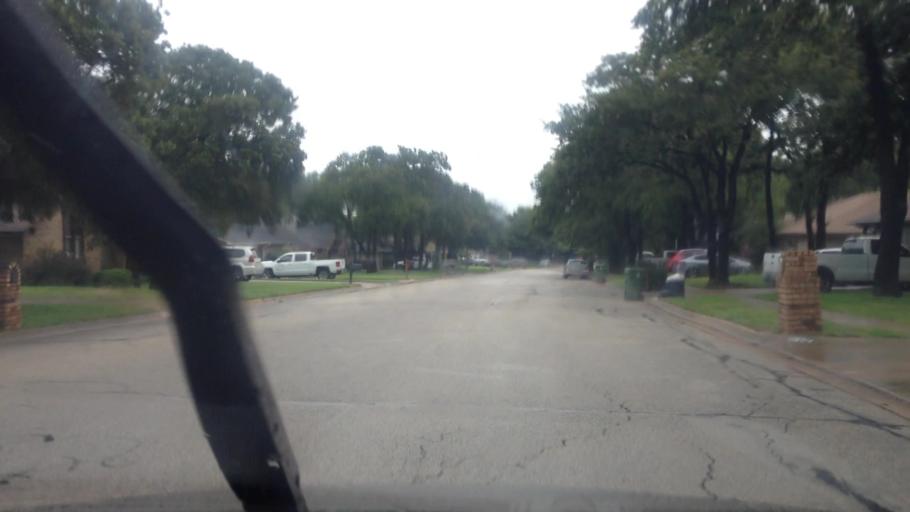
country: US
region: Texas
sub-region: Tarrant County
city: Watauga
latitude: 32.8819
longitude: -97.2336
